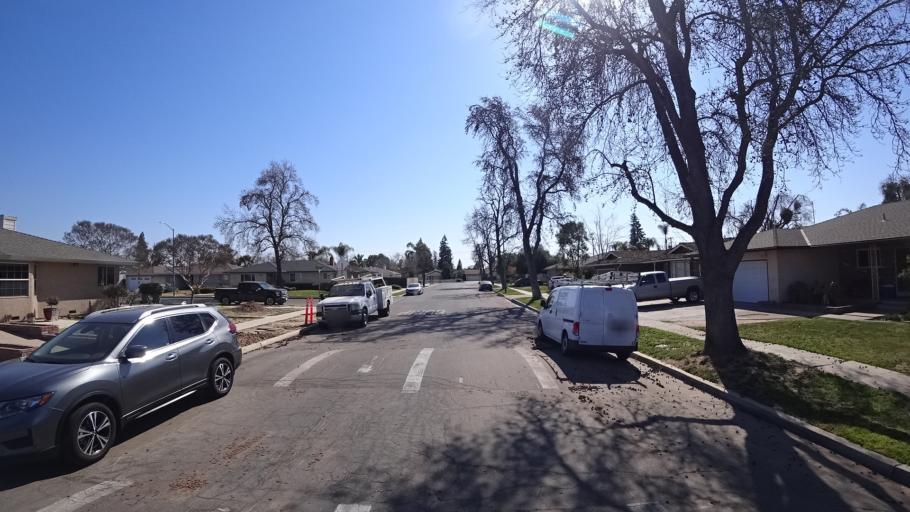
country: US
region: California
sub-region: Fresno County
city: Clovis
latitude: 36.8313
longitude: -119.7792
